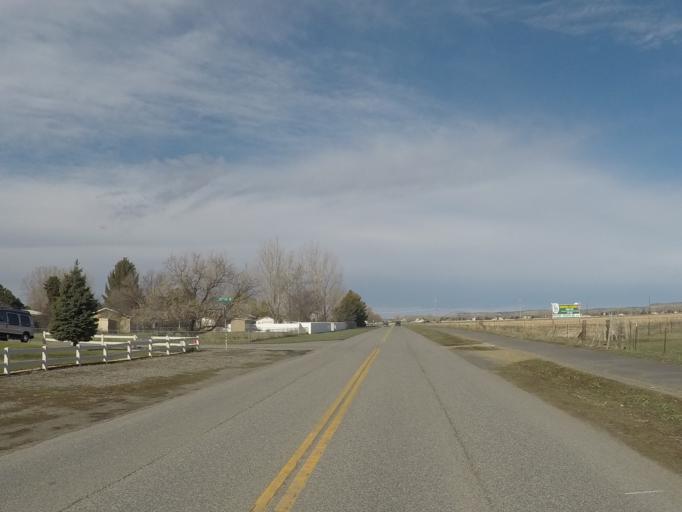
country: US
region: Montana
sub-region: Yellowstone County
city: Billings
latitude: 45.7769
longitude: -108.6105
